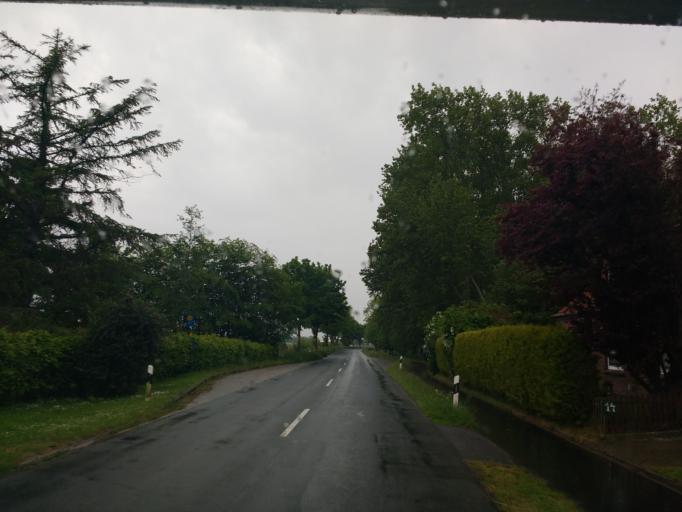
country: DE
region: Lower Saxony
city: Schillig
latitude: 53.7065
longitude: 7.9532
